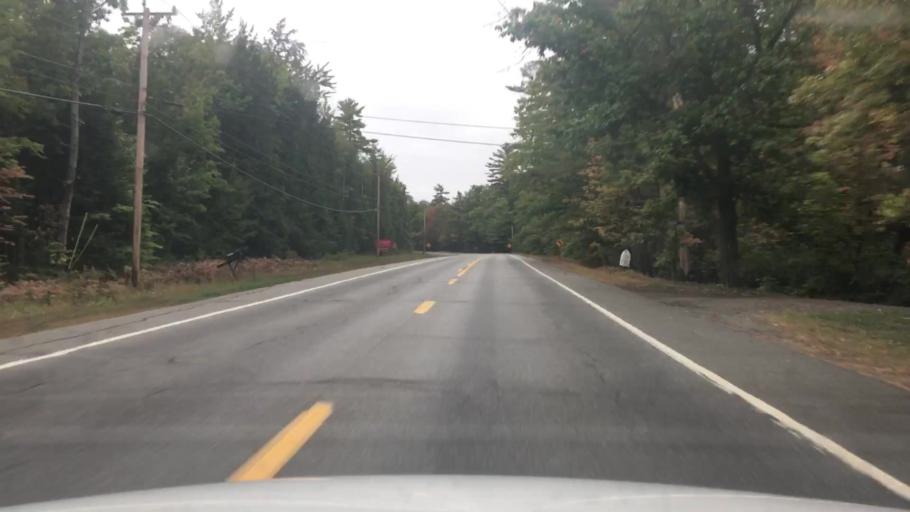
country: US
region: Maine
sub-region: Kennebec County
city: Rome
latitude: 44.5194
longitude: -69.8786
